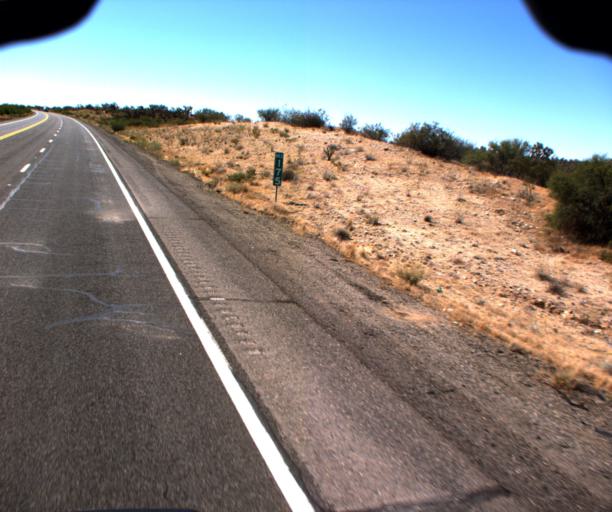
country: US
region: Arizona
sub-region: Yavapai County
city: Congress
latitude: 34.1955
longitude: -113.0578
